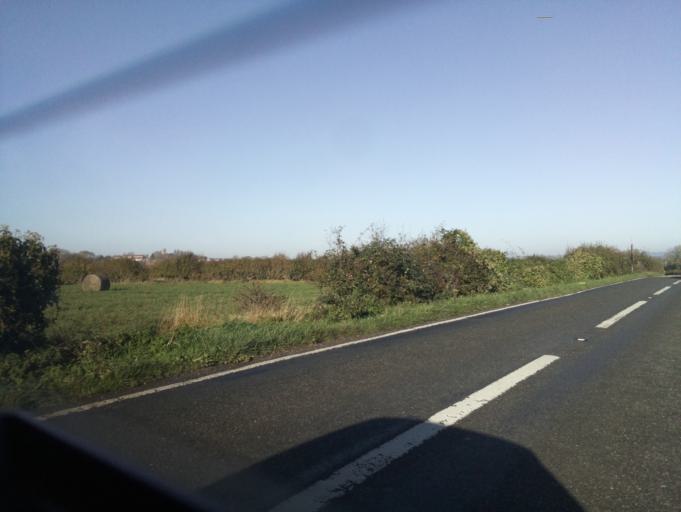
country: GB
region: England
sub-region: Somerset
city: Westonzoyland
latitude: 51.0885
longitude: -2.8809
